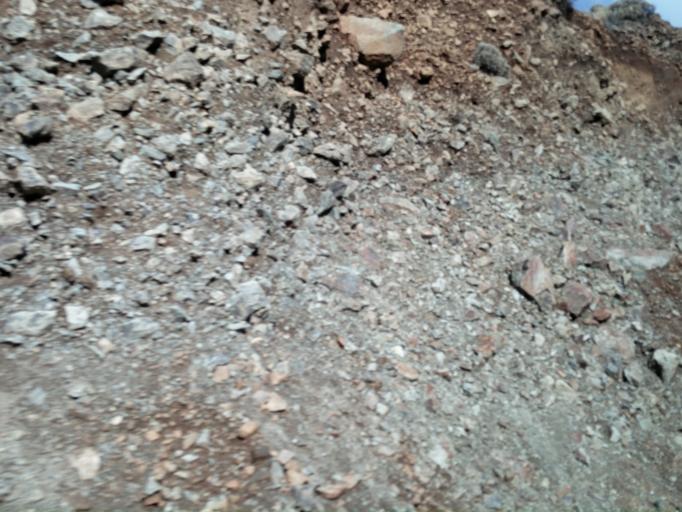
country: ES
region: Canary Islands
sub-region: Provincia de Santa Cruz de Tenerife
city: Vilaflor
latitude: 28.2158
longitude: -16.6267
